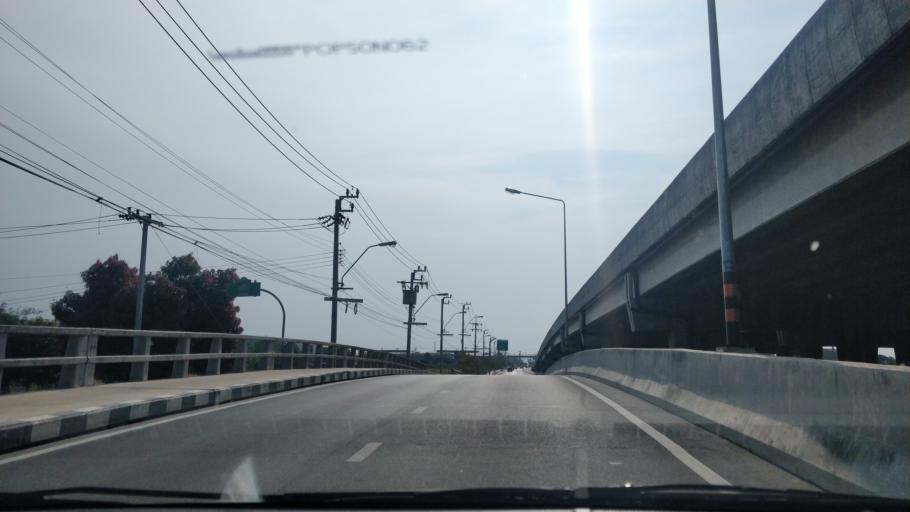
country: TH
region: Bangkok
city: Saphan Sung
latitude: 13.7545
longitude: 100.7241
